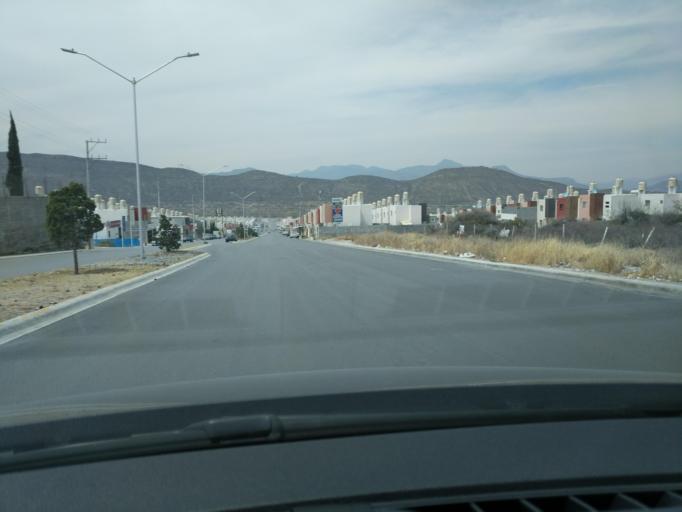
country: MX
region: Coahuila
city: Saltillo
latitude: 25.3624
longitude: -101.0308
